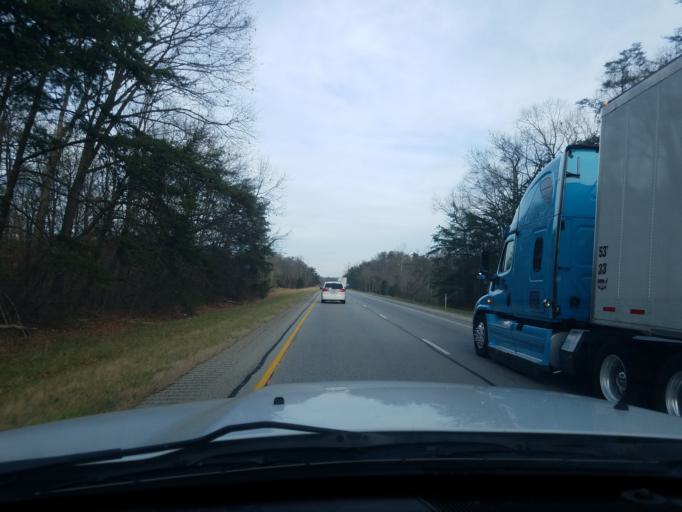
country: US
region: Indiana
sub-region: Floyd County
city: Georgetown
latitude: 38.2785
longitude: -85.9516
